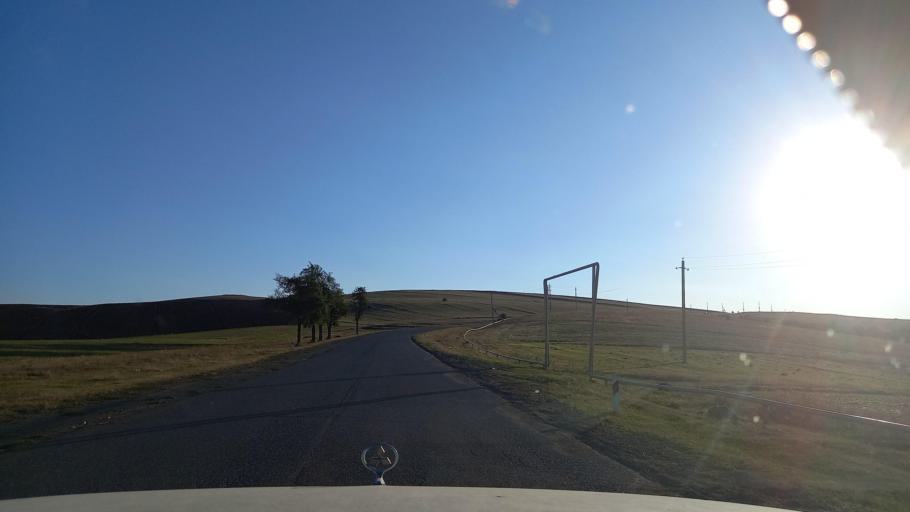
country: AZ
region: Shamkir Rayon
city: Shamkhor
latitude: 40.7674
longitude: 45.9534
